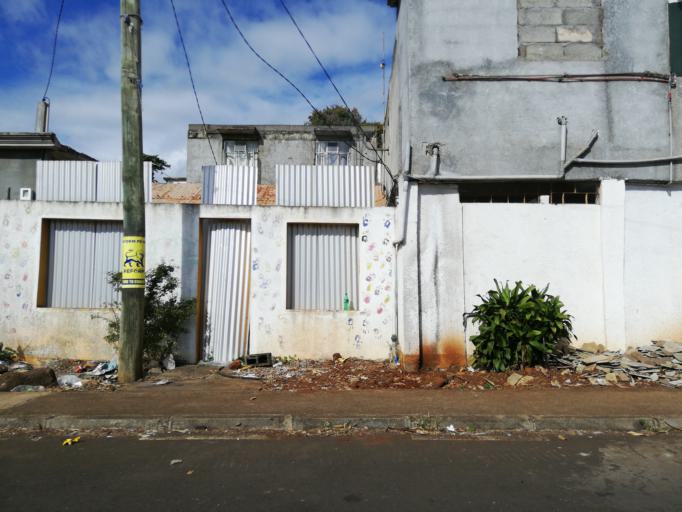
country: MU
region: Black River
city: Gros Cailloux
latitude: -20.2241
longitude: 57.4544
